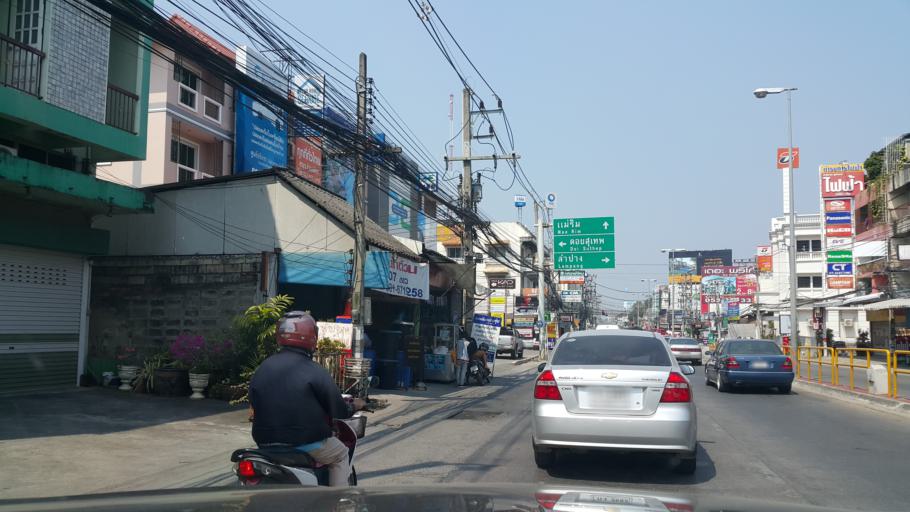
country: TH
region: Chiang Mai
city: Chiang Mai
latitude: 18.8100
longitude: 98.9847
